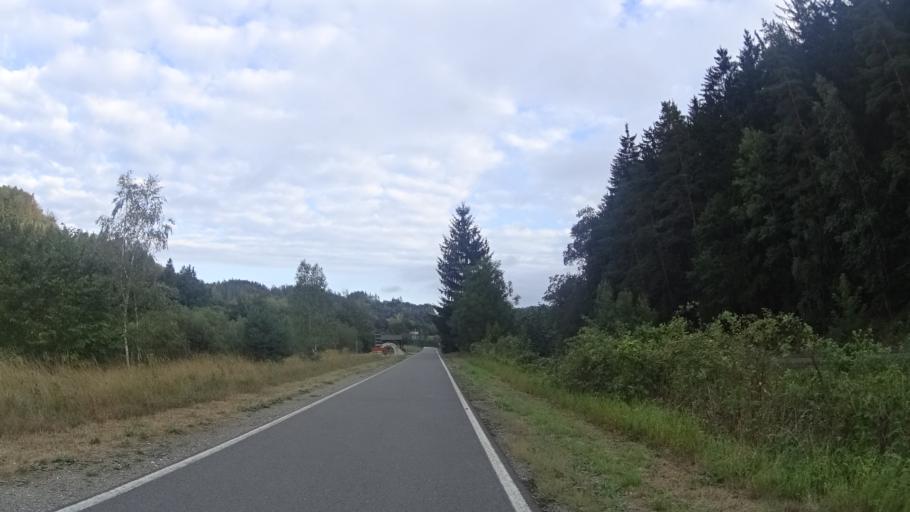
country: CZ
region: Olomoucky
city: Zabreh
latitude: 49.8608
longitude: 16.8209
